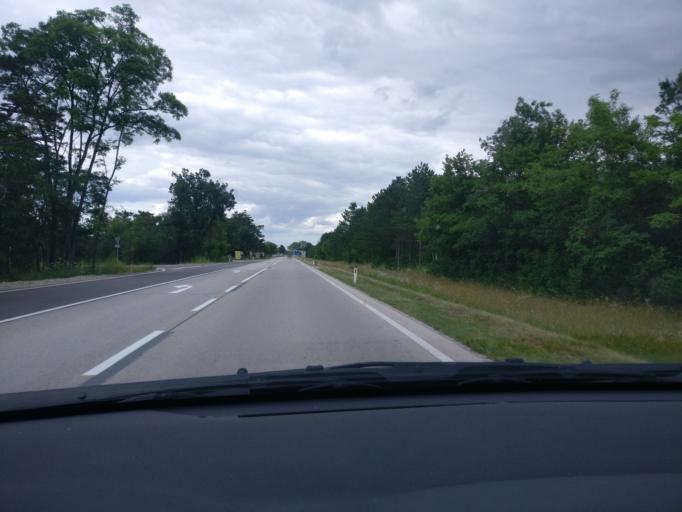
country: AT
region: Lower Austria
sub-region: Wiener Neustadt Stadt
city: Wiener Neustadt
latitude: 47.7801
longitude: 16.2292
